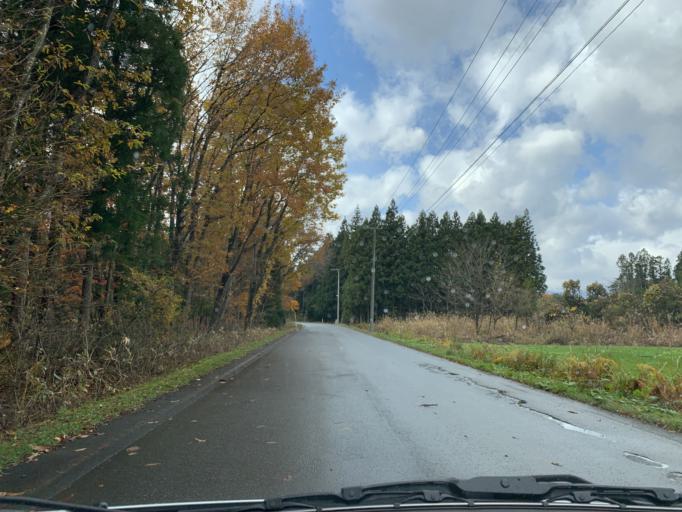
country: JP
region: Iwate
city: Mizusawa
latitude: 39.1067
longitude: 140.9869
